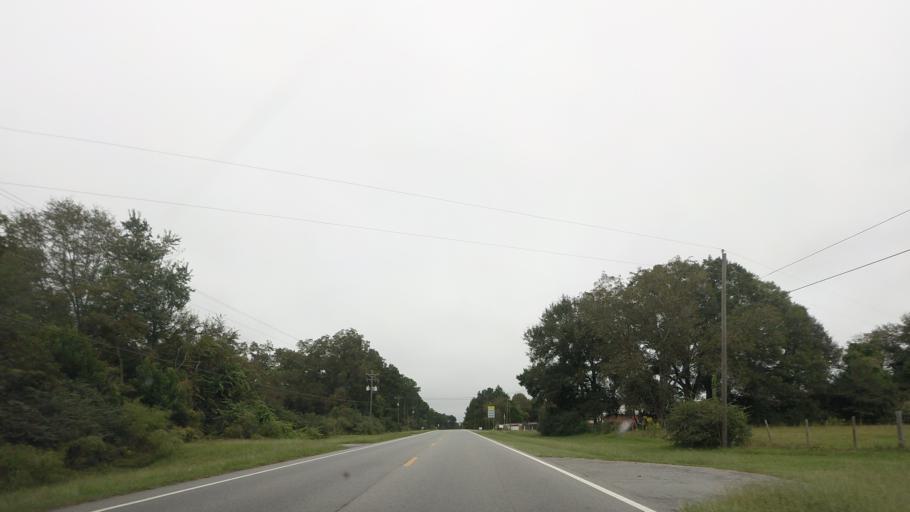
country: US
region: Georgia
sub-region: Berrien County
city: Nashville
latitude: 31.2304
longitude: -83.2468
